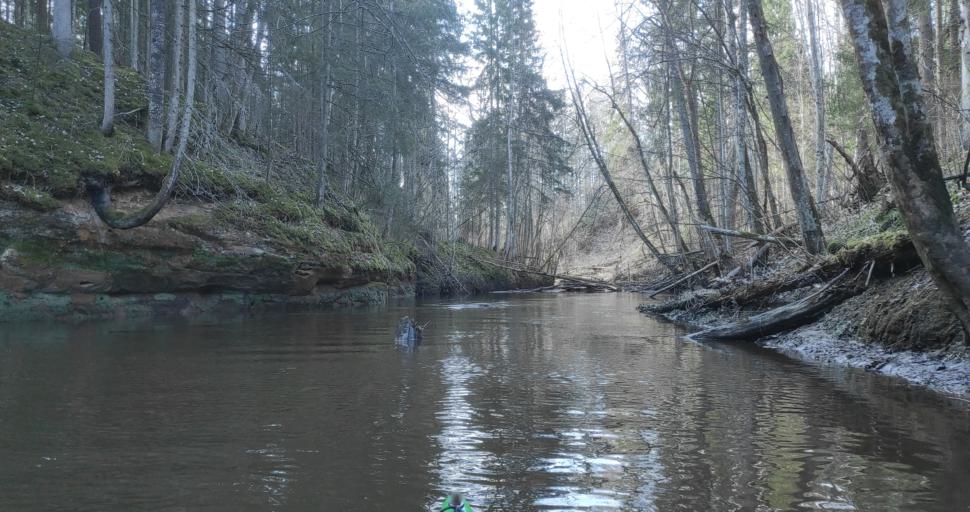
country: LV
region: Talsu Rajons
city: Valdemarpils
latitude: 57.4441
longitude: 22.6586
